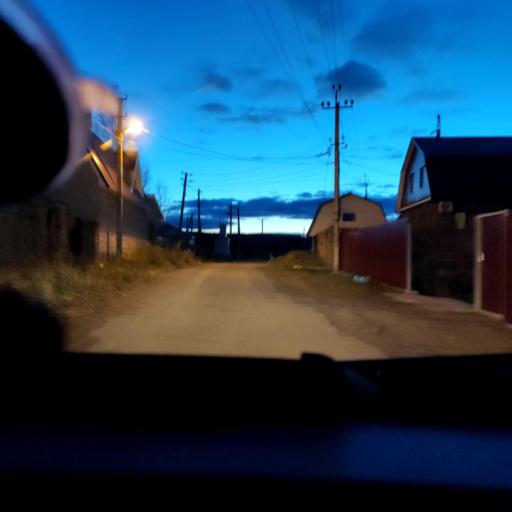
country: RU
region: Bashkortostan
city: Avdon
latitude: 54.6860
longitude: 55.7817
